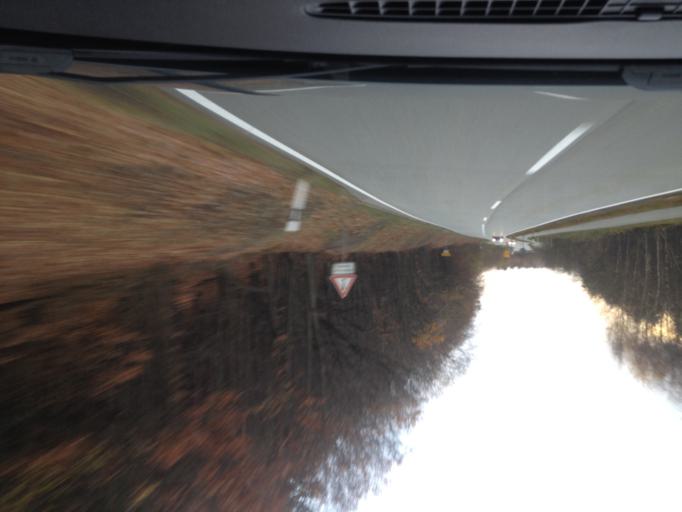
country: DE
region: Rheinland-Pfalz
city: Fischbach
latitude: 49.4434
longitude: 7.9227
